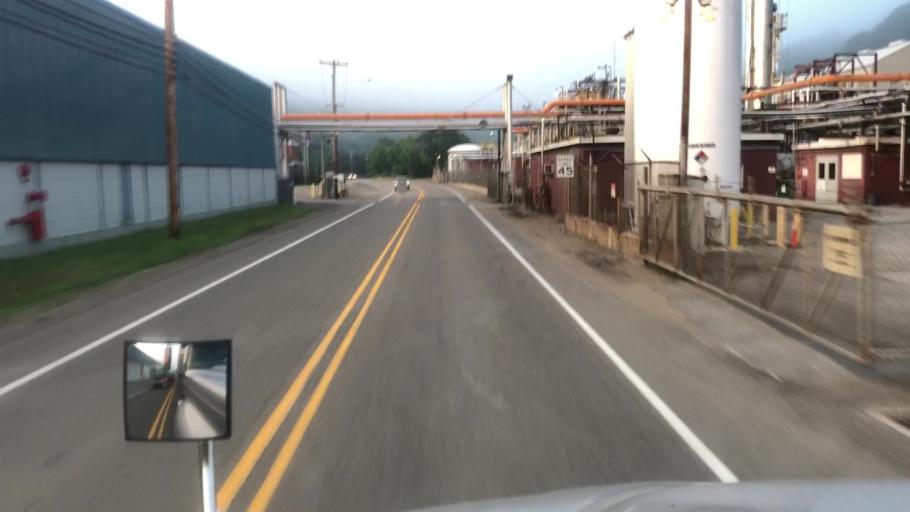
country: US
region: Pennsylvania
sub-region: Venango County
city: Hasson Heights
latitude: 41.4538
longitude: -79.6897
